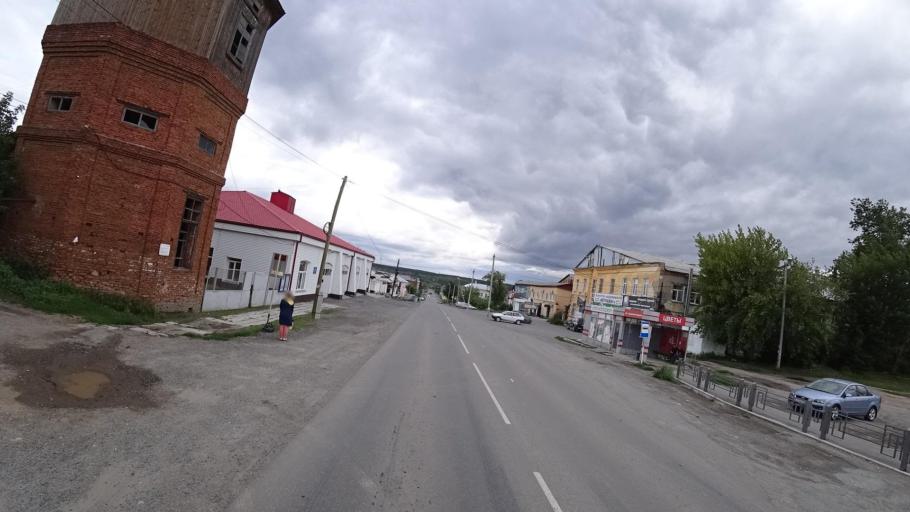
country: RU
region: Sverdlovsk
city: Kamyshlov
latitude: 56.8475
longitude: 62.6994
